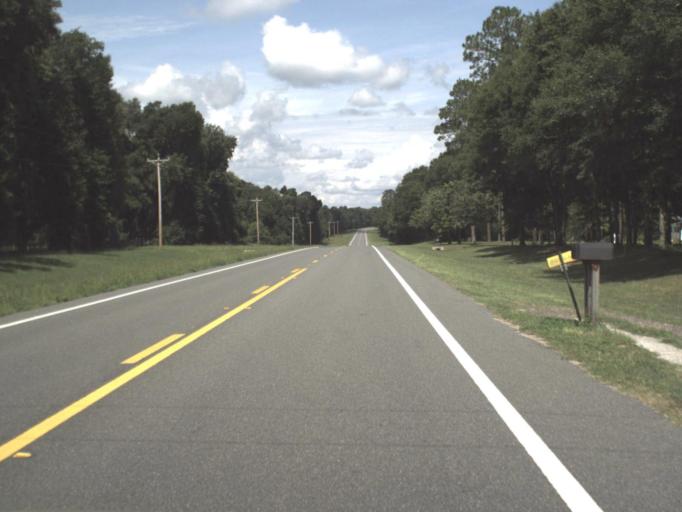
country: US
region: Florida
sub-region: Alachua County
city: Alachua
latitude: 29.8400
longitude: -82.3723
